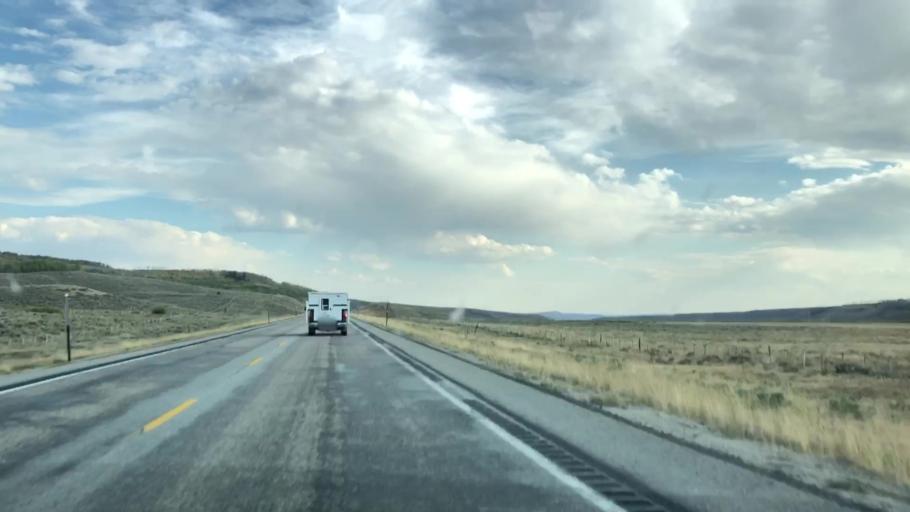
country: US
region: Wyoming
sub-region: Sublette County
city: Pinedale
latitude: 43.0973
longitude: -110.1678
